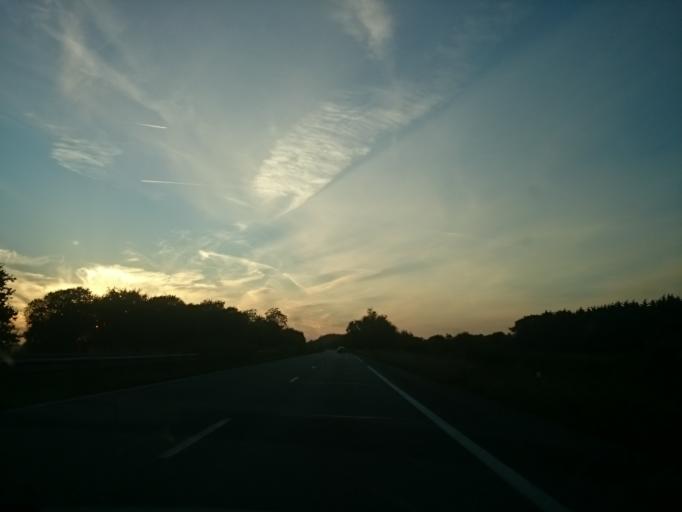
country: FR
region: Brittany
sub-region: Departement du Finistere
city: Saint-Yvi
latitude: 47.9621
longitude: -3.9639
